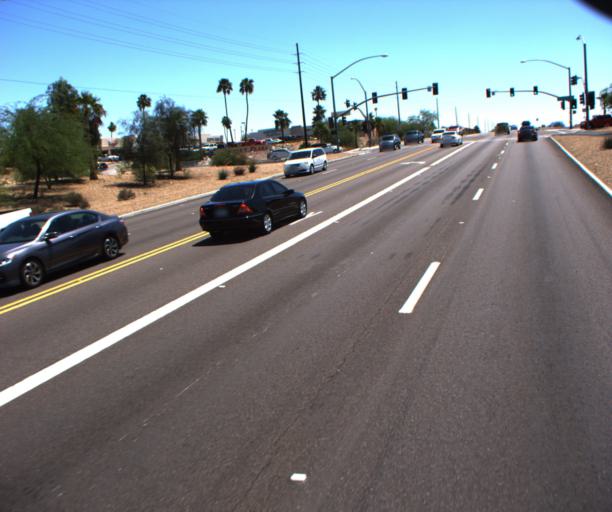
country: US
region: Arizona
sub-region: Mohave County
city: Lake Havasu City
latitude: 34.4727
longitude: -114.3446
